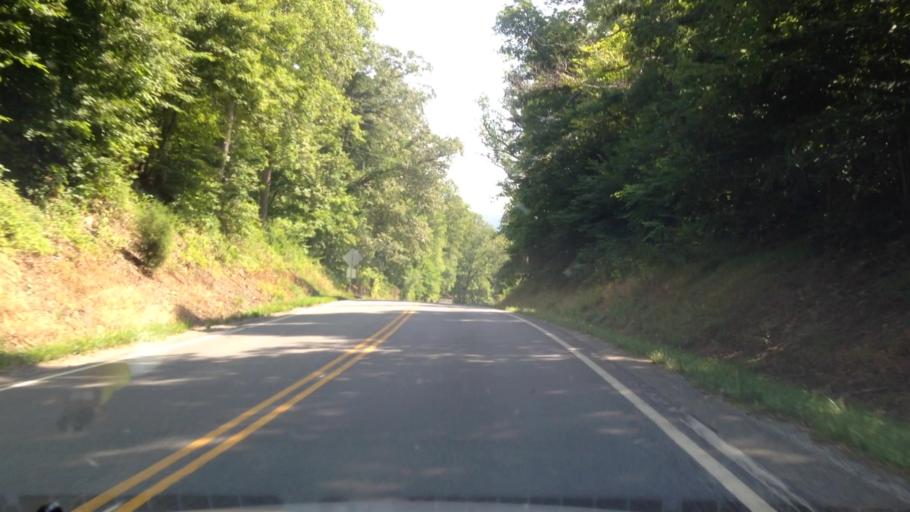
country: US
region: Virginia
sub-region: Patrick County
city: Stuart
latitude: 36.5925
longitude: -80.3168
